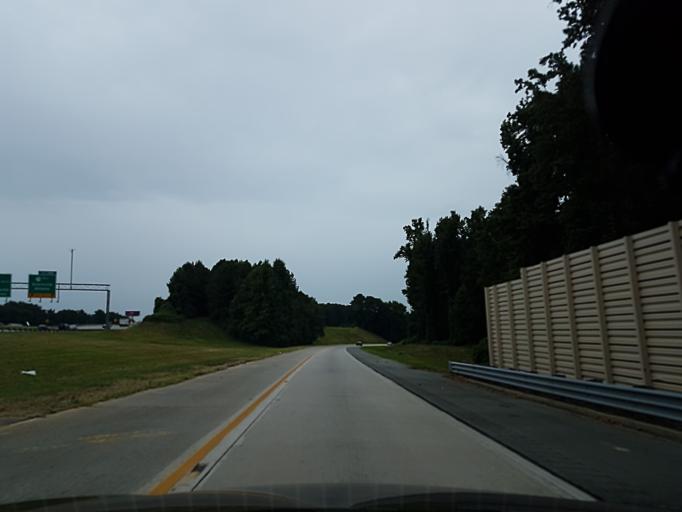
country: US
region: Georgia
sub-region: DeKalb County
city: Clarkston
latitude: 33.8186
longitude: -84.2527
